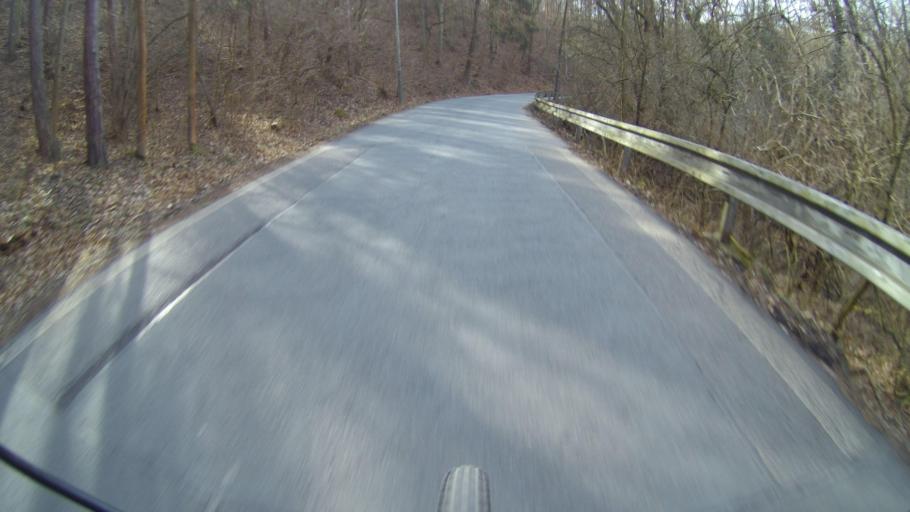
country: CZ
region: Central Bohemia
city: Roztoky
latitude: 50.1358
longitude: 14.3988
